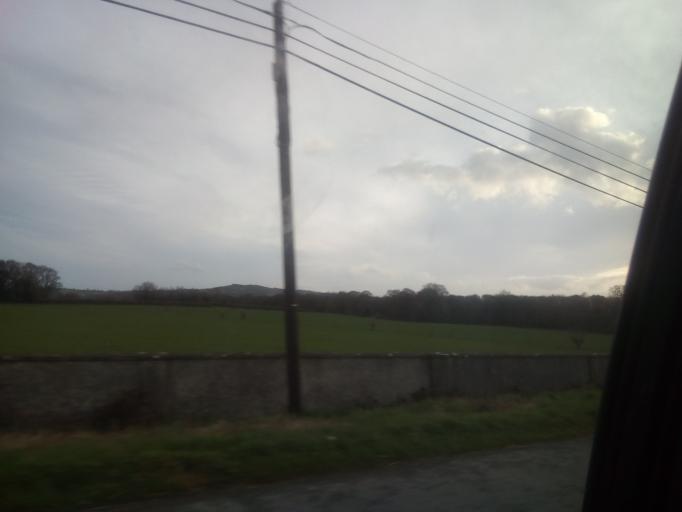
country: IE
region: Leinster
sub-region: Laois
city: Abbeyleix
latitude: 52.8583
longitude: -7.3776
